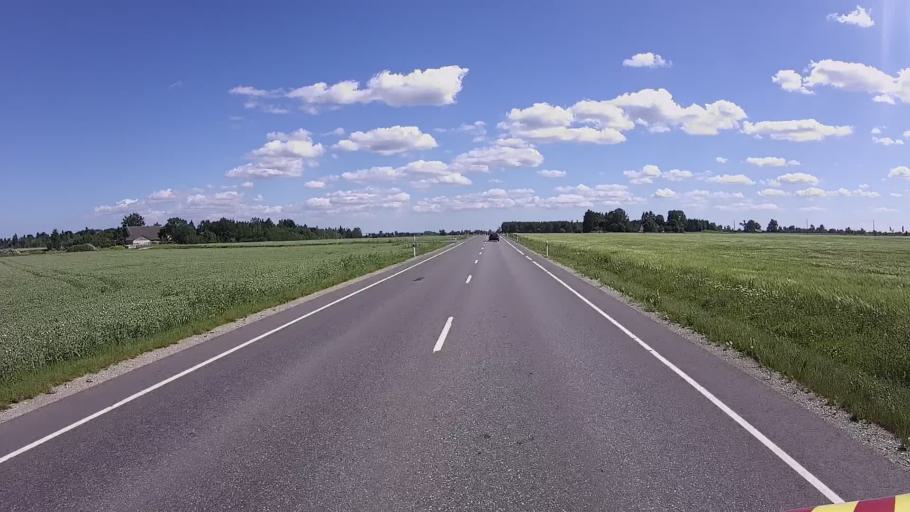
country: EE
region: Ida-Virumaa
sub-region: Johvi vald
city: Johvi
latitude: 59.3391
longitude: 27.3653
